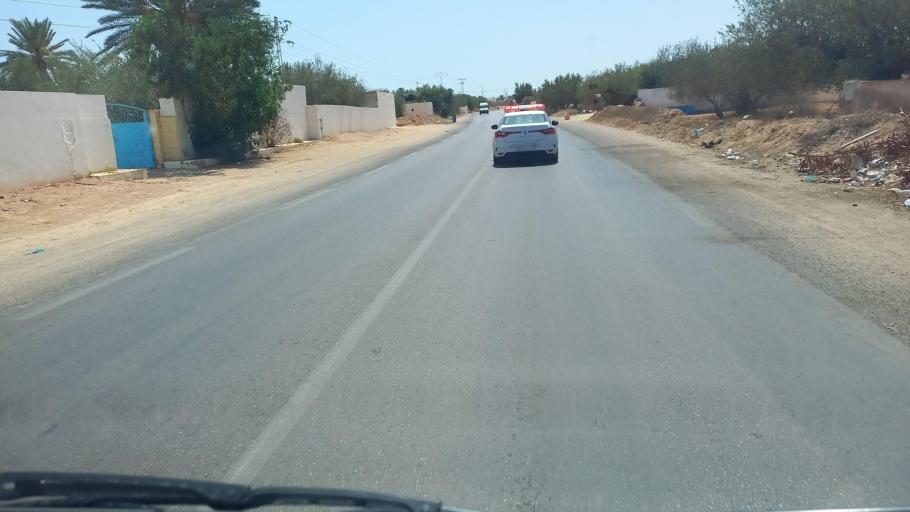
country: TN
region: Madanin
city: Midoun
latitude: 33.7685
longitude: 10.9016
